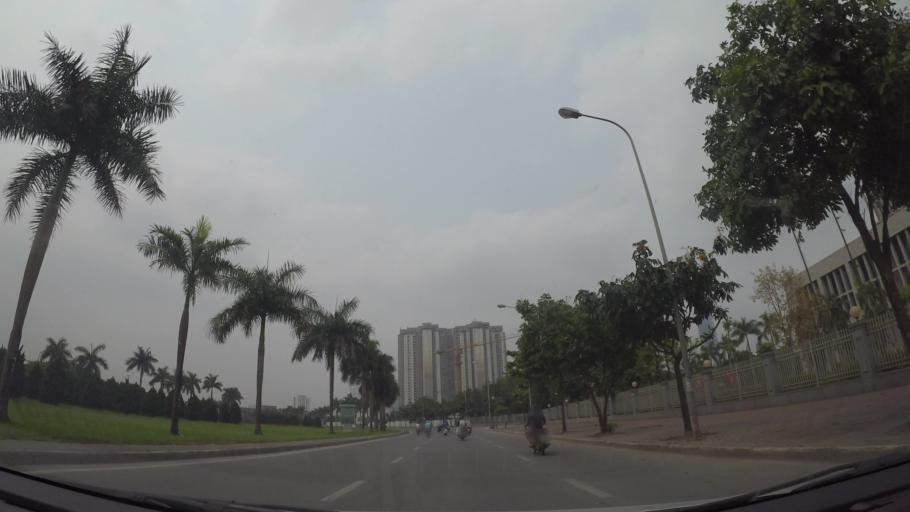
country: VN
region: Ha Noi
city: Thanh Xuan
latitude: 21.0069
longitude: 105.7742
